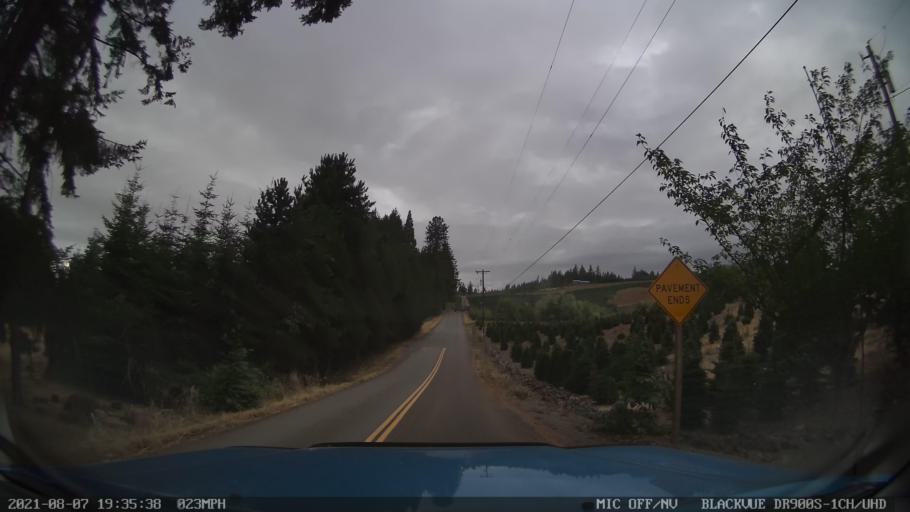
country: US
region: Oregon
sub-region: Marion County
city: Silverton
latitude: 44.9281
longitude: -122.6567
